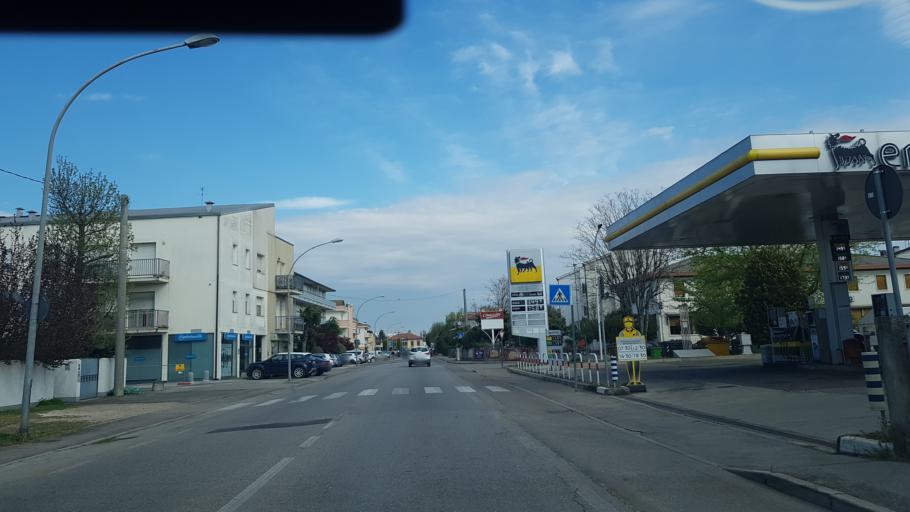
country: IT
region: Veneto
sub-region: Provincia di Rovigo
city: Rovigo
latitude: 45.0712
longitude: 11.8004
